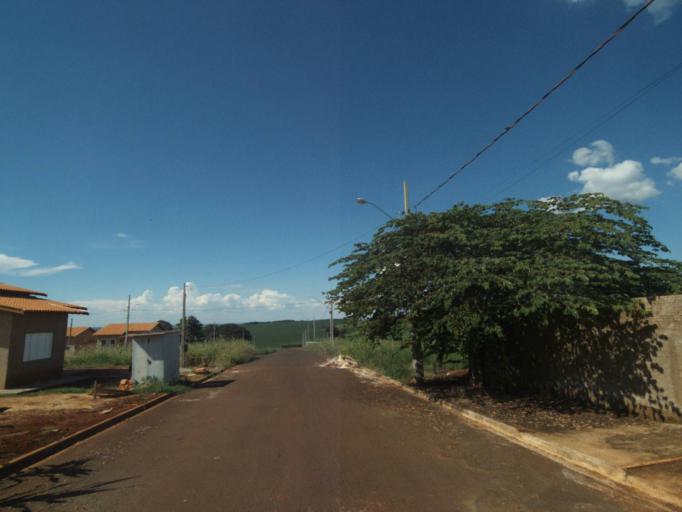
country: BR
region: Parana
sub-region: Sertanopolis
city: Sertanopolis
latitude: -23.0367
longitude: -50.8100
